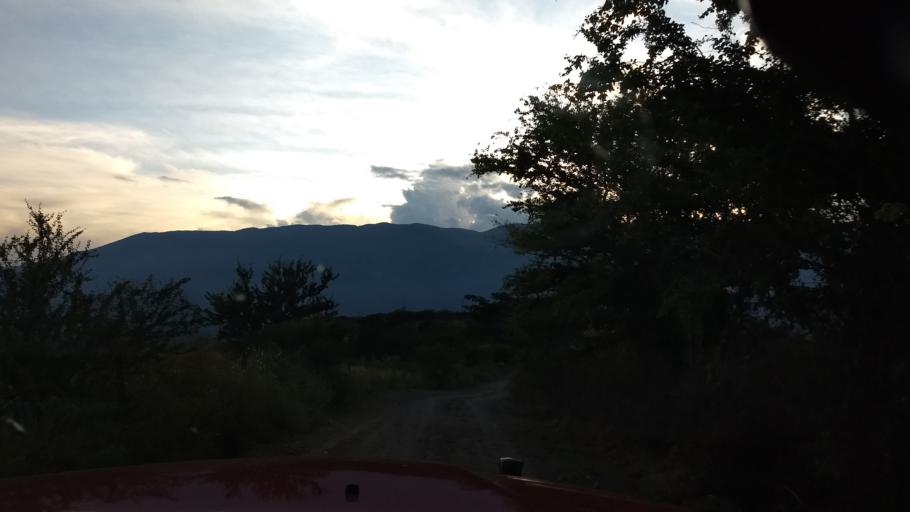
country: MX
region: Colima
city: Suchitlan
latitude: 19.4849
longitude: -103.7945
